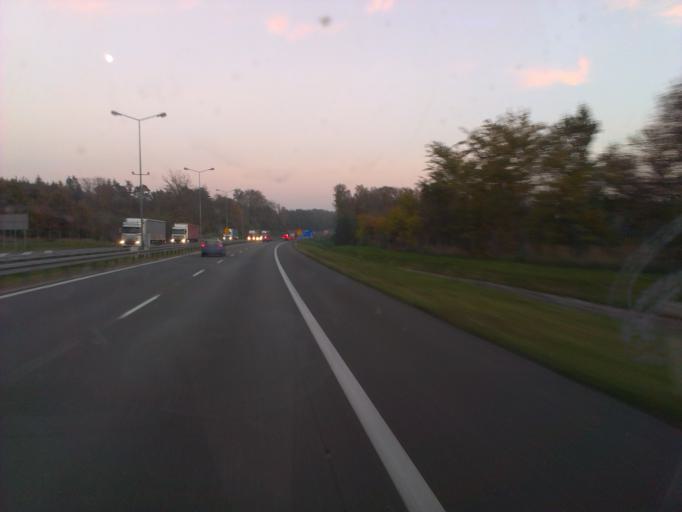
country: PL
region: Opole Voivodeship
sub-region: Powiat strzelecki
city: Ujazd
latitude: 50.4440
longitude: 18.3538
